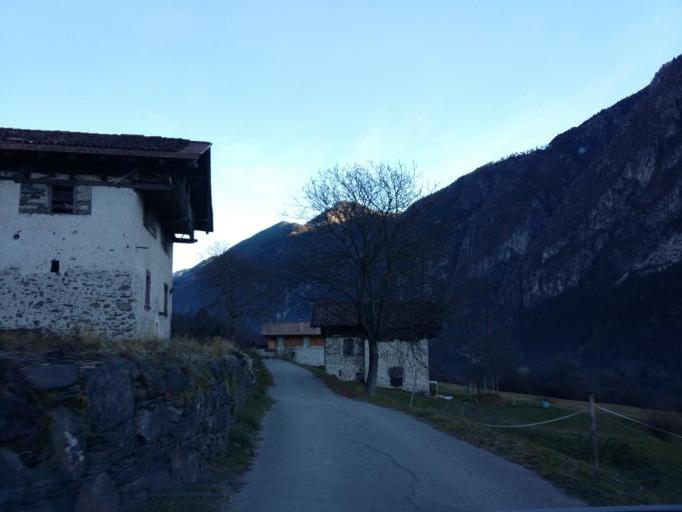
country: IT
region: Trentino-Alto Adige
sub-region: Provincia di Trento
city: Condino
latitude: 45.8698
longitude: 10.5790
